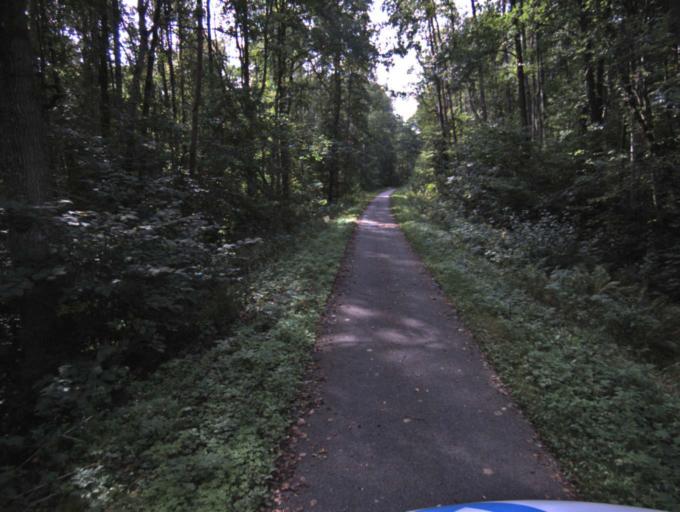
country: SE
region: Vaestra Goetaland
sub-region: Tranemo Kommun
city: Limmared
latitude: 57.6443
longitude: 13.3595
